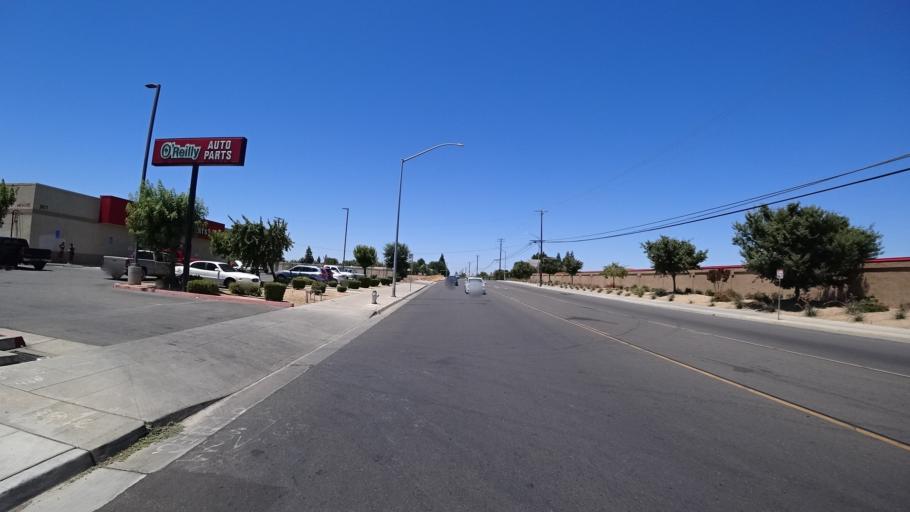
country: US
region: California
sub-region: Fresno County
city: West Park
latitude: 36.7719
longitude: -119.8459
